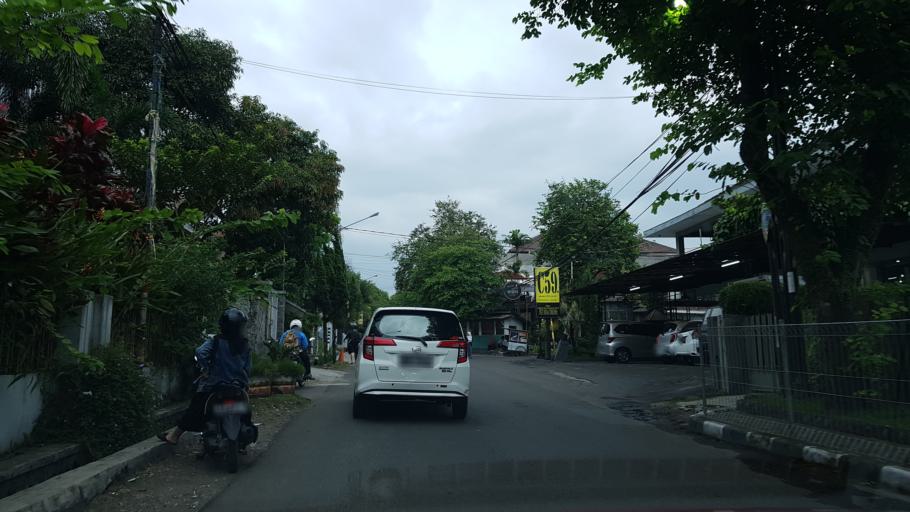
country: ID
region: West Java
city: Bandung
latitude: -6.8989
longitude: 107.6203
